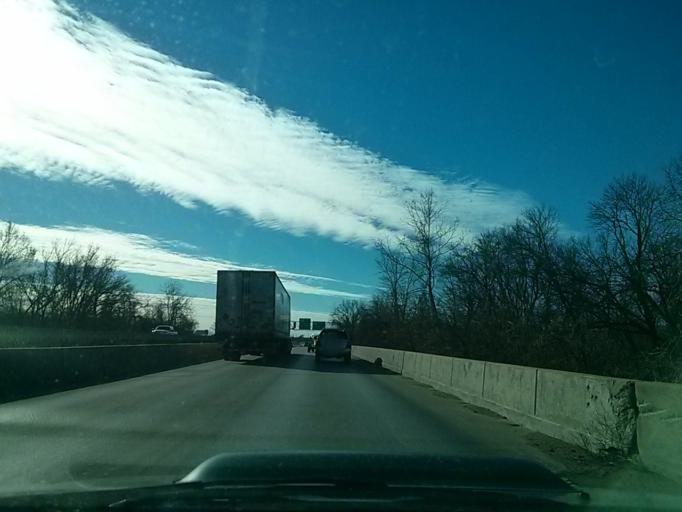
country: US
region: Oklahoma
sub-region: Tulsa County
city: Jenks
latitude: 36.0170
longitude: -96.0118
